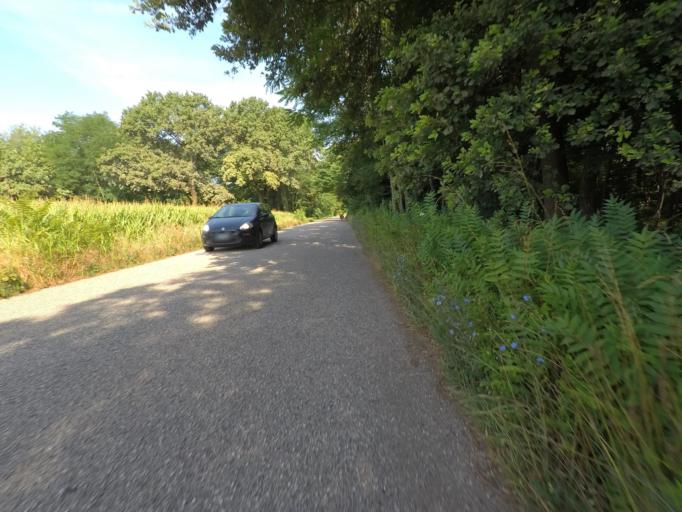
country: IT
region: Friuli Venezia Giulia
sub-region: Provincia di Udine
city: Colloredo di Prato
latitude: 46.0586
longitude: 13.1139
